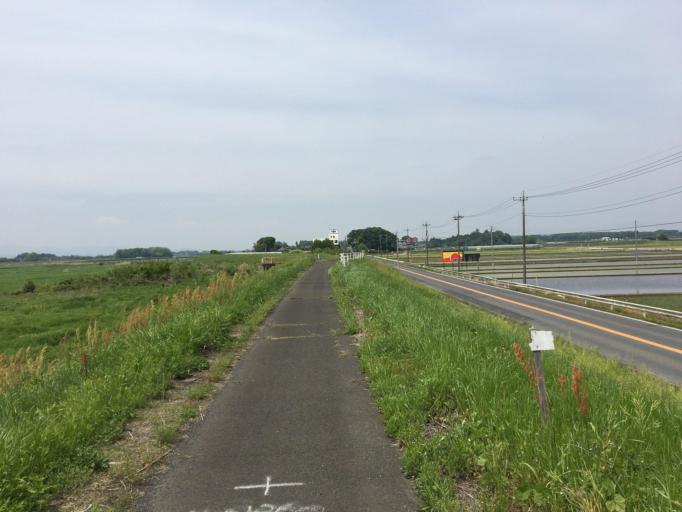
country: JP
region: Tochigi
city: Mibu
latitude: 36.3611
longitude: 139.8066
